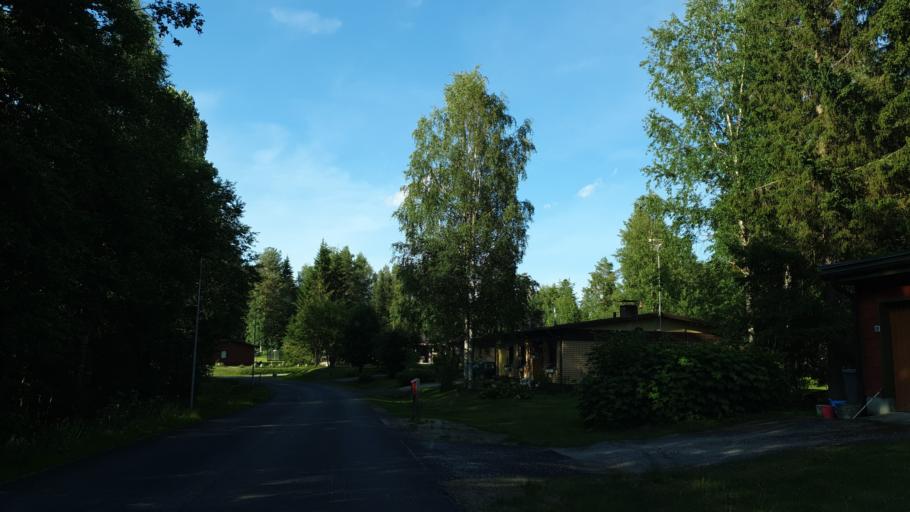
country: FI
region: Kainuu
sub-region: Kehys-Kainuu
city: Kuhmo
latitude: 64.1172
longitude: 29.4937
